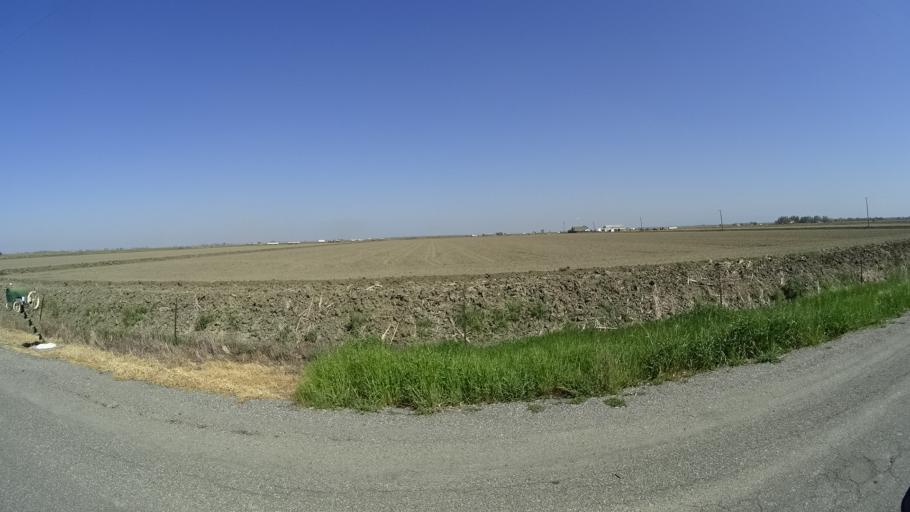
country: US
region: California
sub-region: Glenn County
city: Willows
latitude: 39.4812
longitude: -122.0529
